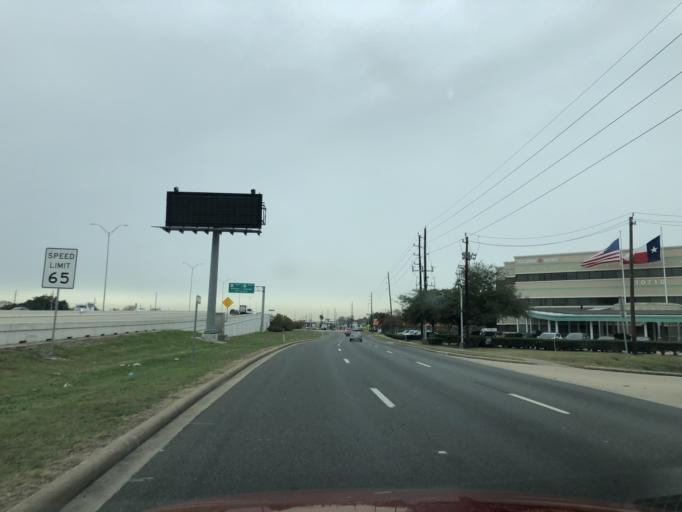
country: US
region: Texas
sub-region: Fort Bend County
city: Missouri City
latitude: 29.6423
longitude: -95.5364
